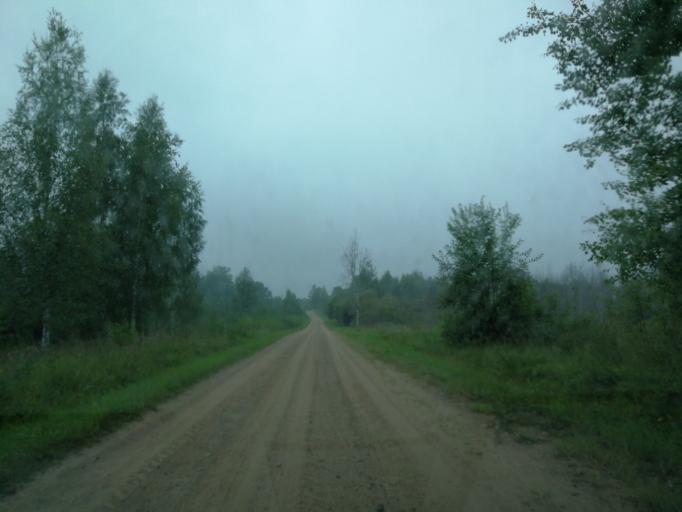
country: LV
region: Preilu Rajons
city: Jaunaglona
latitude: 56.3188
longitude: 27.0129
